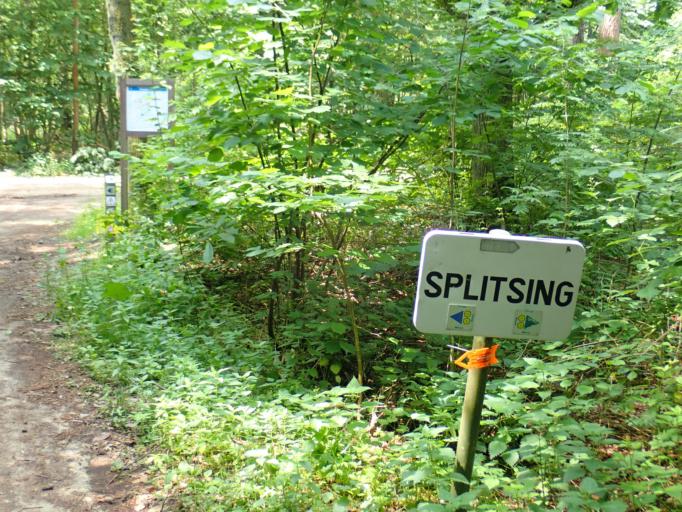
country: BE
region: Flanders
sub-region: Provincie Antwerpen
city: Kasterlee
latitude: 51.2150
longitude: 4.9017
